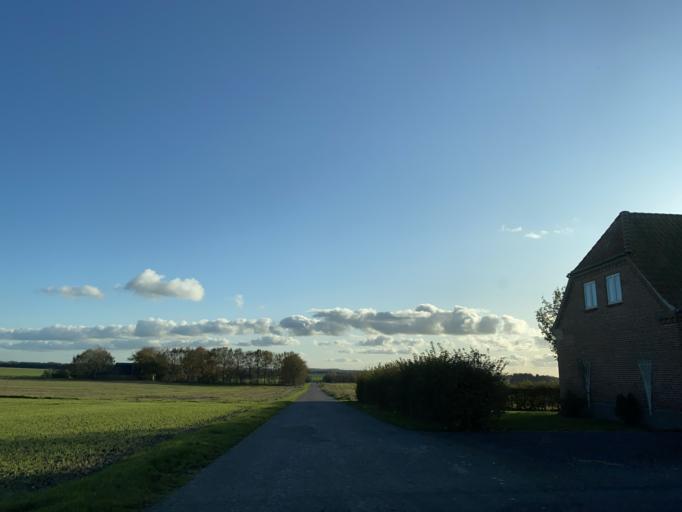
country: DK
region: Central Jutland
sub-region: Viborg Kommune
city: Bjerringbro
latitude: 56.3321
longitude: 9.7092
